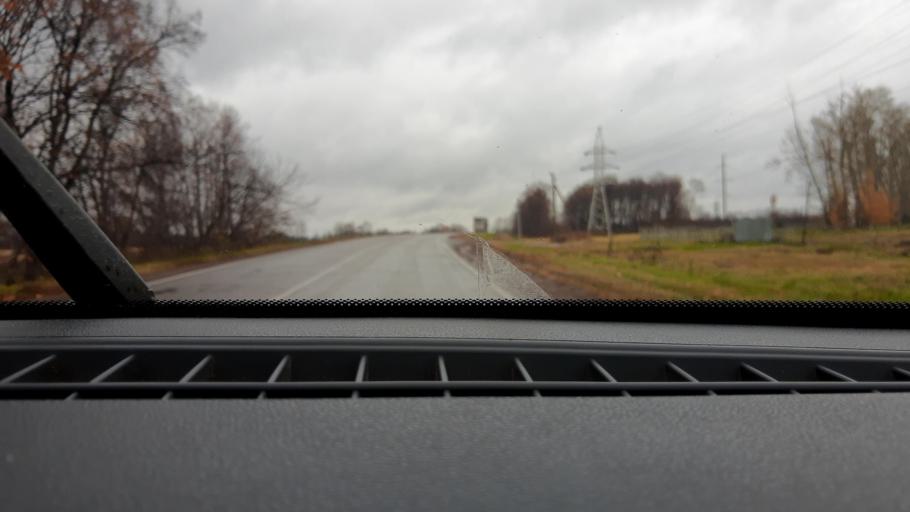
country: RU
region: Bashkortostan
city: Mikhaylovka
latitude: 54.8327
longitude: 55.7894
